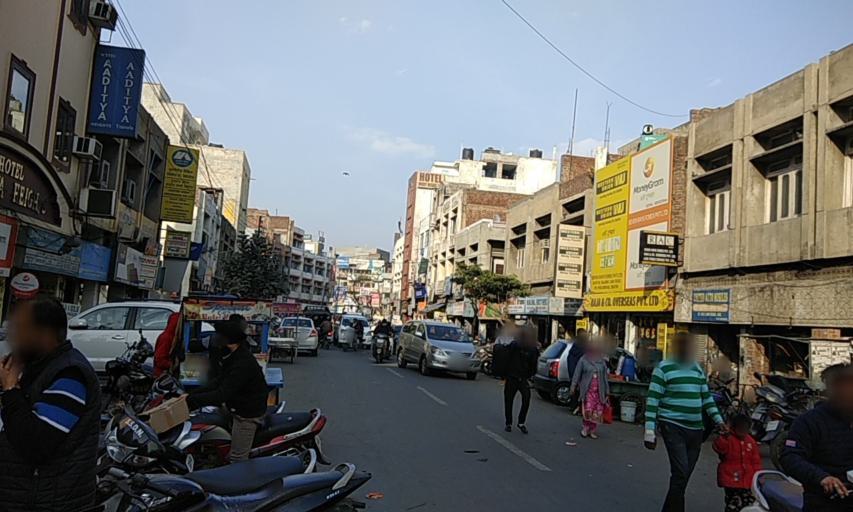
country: IN
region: Punjab
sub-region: Amritsar
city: Amritsar
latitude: 31.6355
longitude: 74.8679
